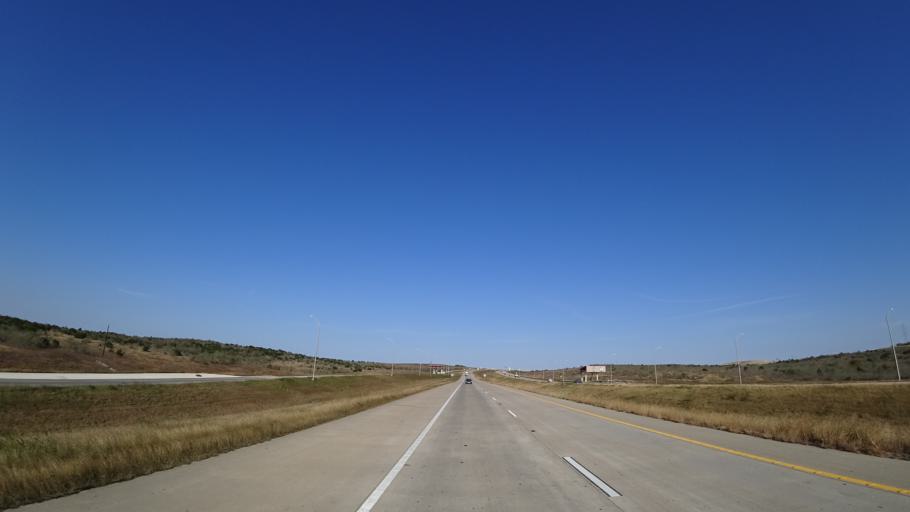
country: US
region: Texas
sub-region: Travis County
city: Manor
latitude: 30.3245
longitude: -97.5814
